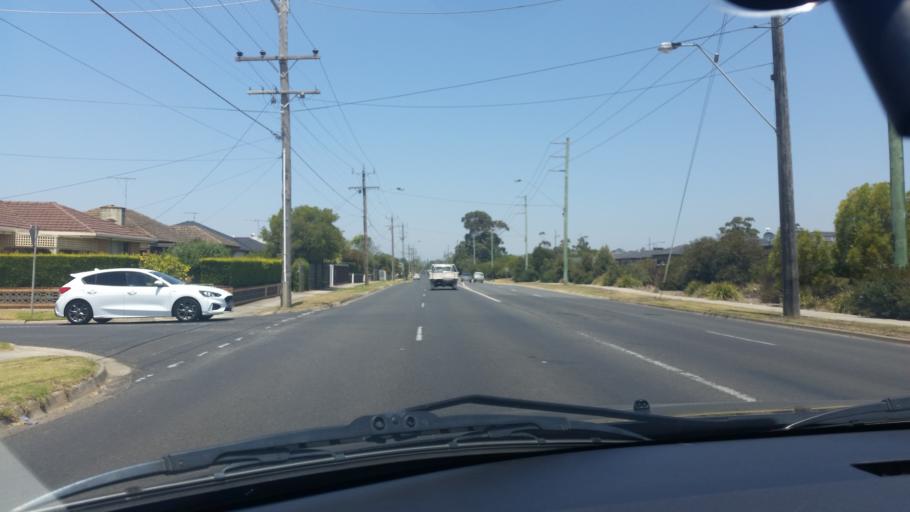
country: AU
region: Victoria
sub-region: Greater Geelong
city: Bell Park
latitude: -38.1170
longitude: 144.3422
